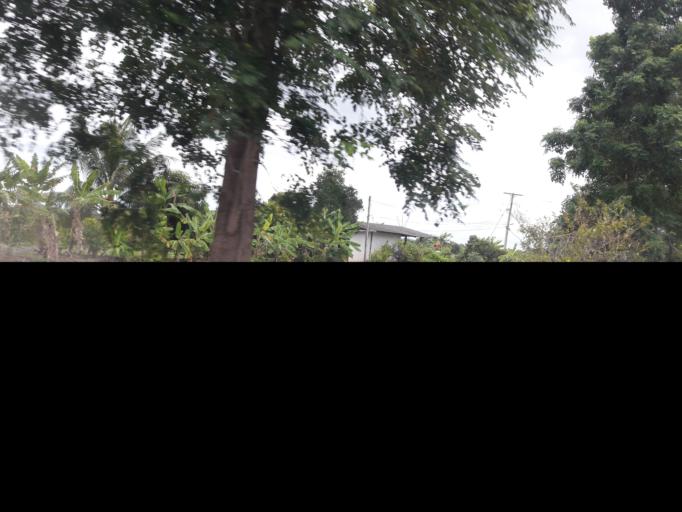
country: TH
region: Ratchaburi
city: Bang Phae
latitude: 13.6097
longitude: 99.9410
